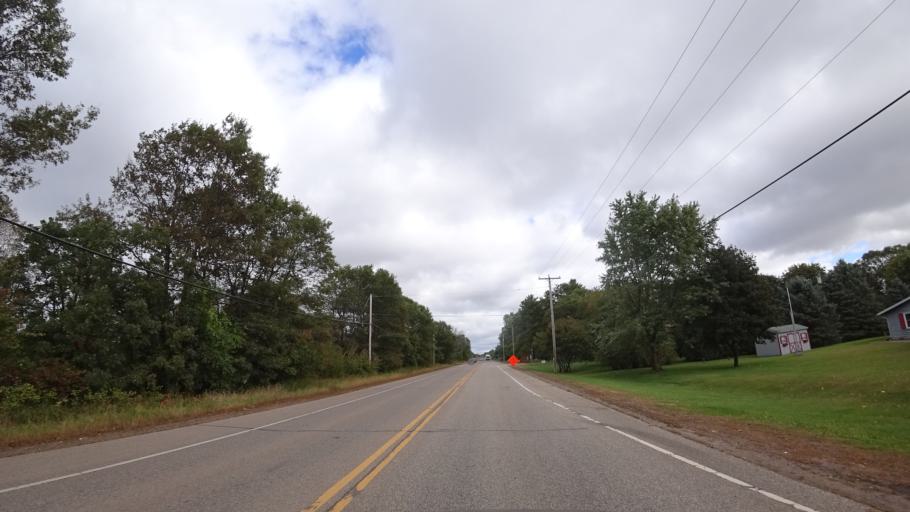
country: US
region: Wisconsin
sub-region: Chippewa County
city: Lake Wissota
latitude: 44.9269
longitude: -91.2973
